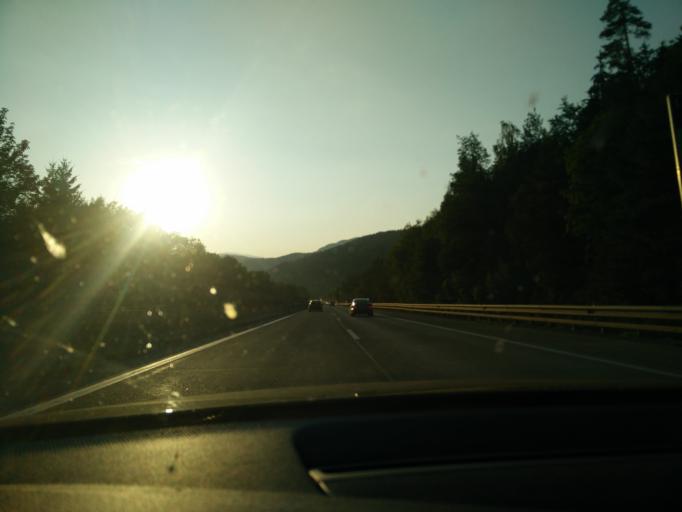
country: AT
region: Carinthia
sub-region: Politischer Bezirk Klagenfurt Land
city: Maria Worth
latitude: 46.6350
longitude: 14.1652
